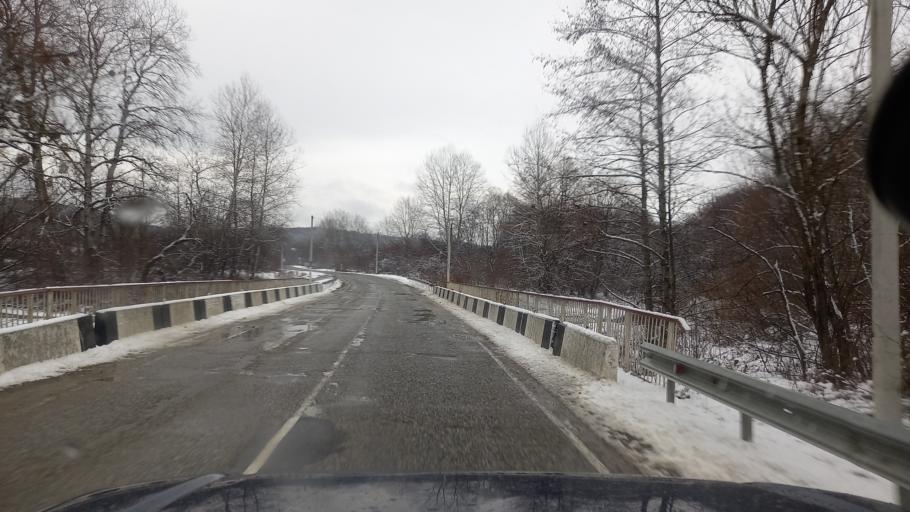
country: RU
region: Adygeya
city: Abadzekhskaya
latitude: 44.3596
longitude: 40.2953
